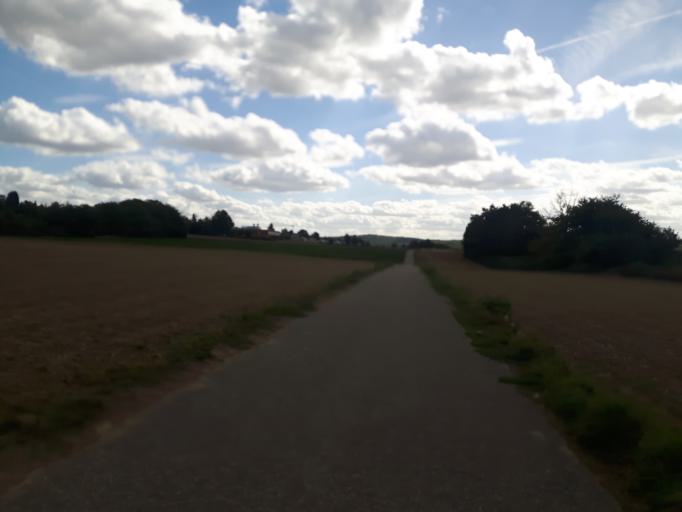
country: DE
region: Baden-Wuerttemberg
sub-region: Regierungsbezirk Stuttgart
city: Flein
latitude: 49.1145
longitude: 9.2108
